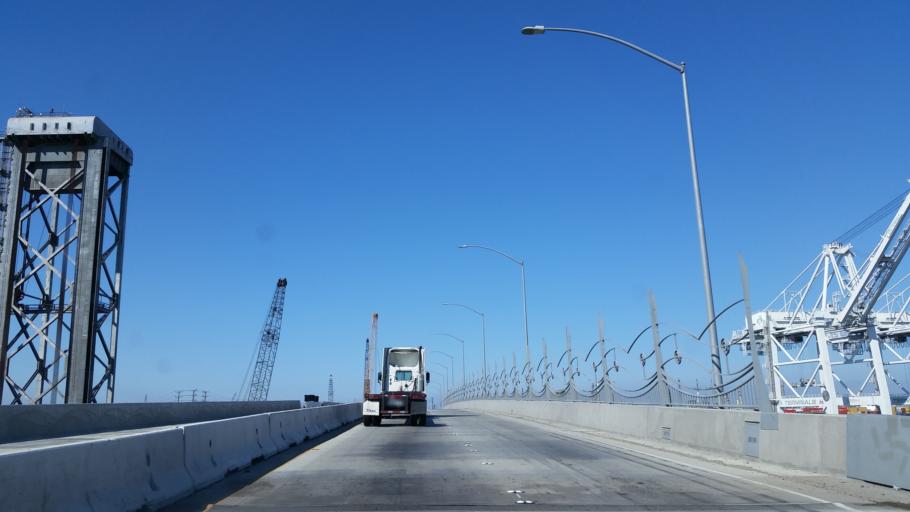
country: US
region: California
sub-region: Los Angeles County
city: Long Beach
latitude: 33.7651
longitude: -118.2393
